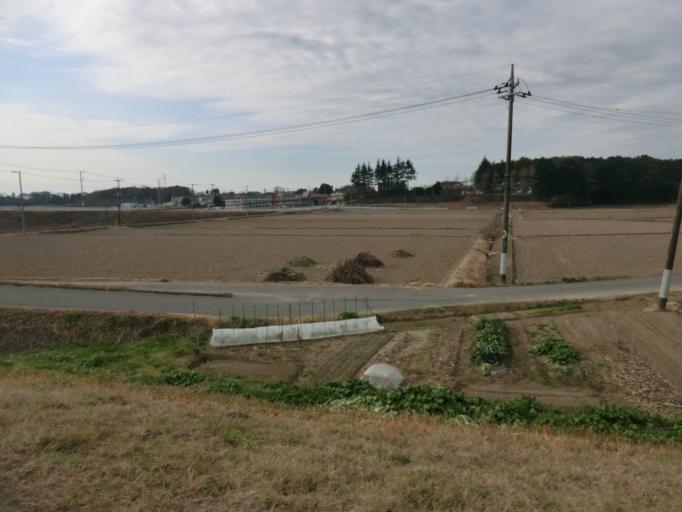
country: JP
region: Ibaraki
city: Mitsukaido
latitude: 35.9862
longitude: 139.9910
